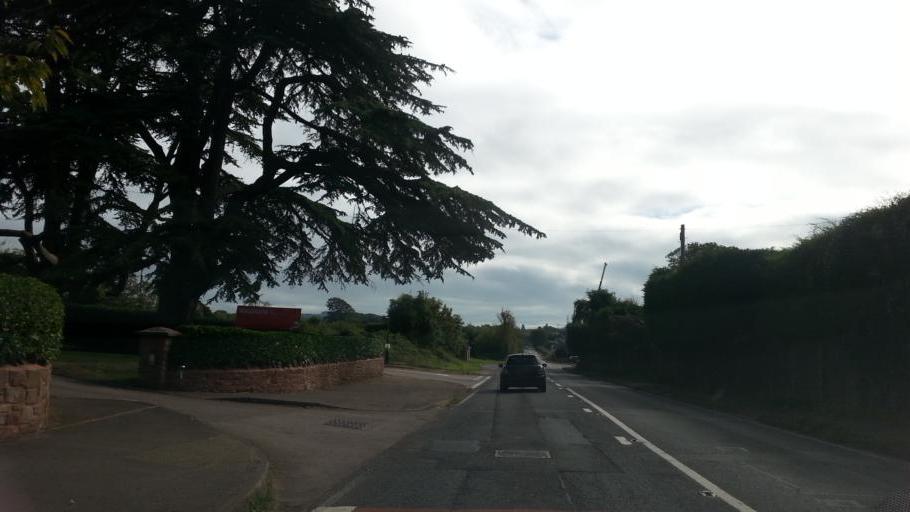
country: GB
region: England
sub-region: Herefordshire
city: Lea
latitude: 51.9069
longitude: -2.5335
